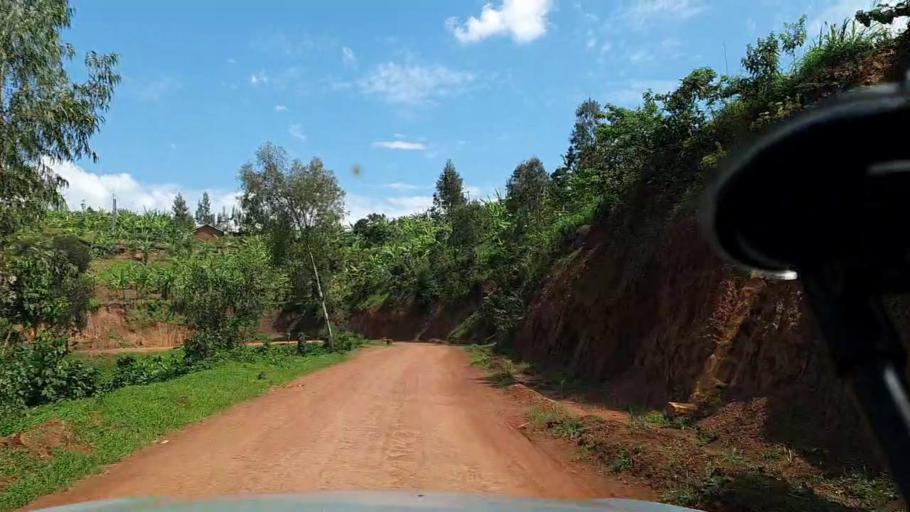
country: RW
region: Kigali
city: Kigali
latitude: -1.8020
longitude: 29.8936
